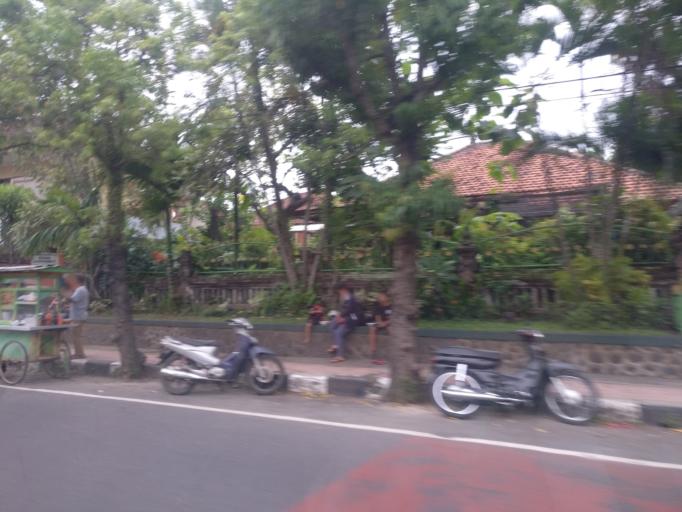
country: ID
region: Bali
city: Banjar Sedang
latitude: -8.5620
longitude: 115.3010
